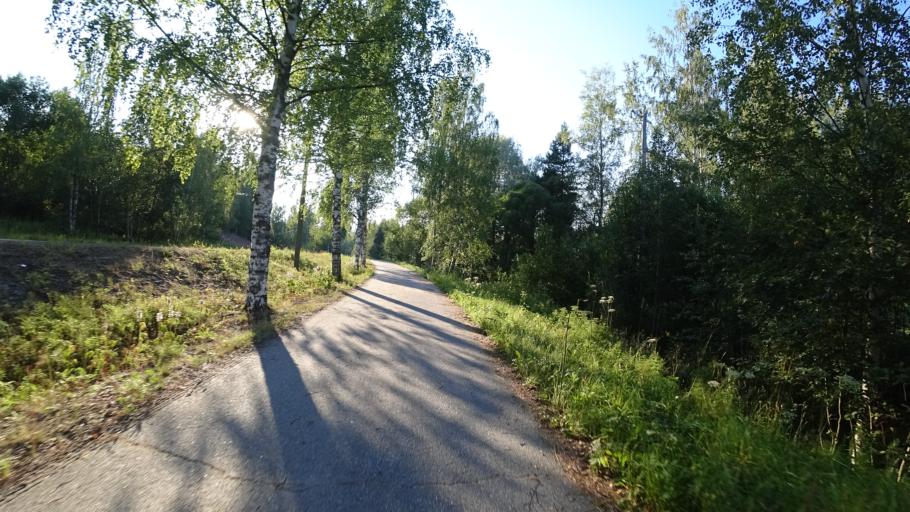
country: FI
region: Pirkanmaa
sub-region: Tampere
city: Nokia
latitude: 61.4728
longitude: 23.3810
